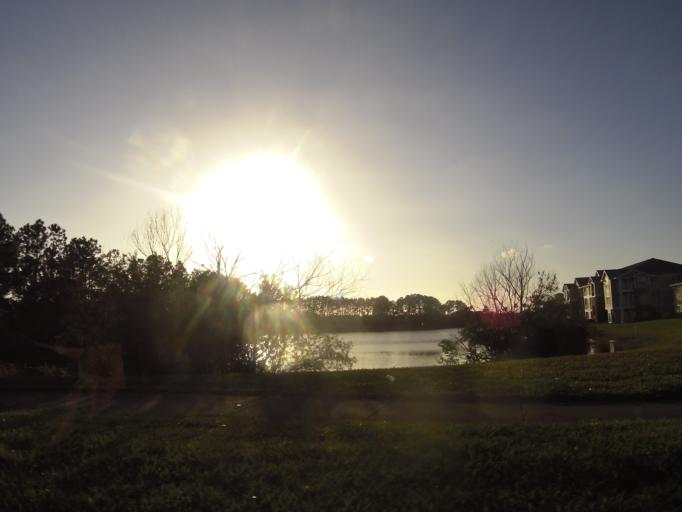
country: US
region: Florida
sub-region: Duval County
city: Jacksonville
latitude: 30.2652
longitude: -81.5504
